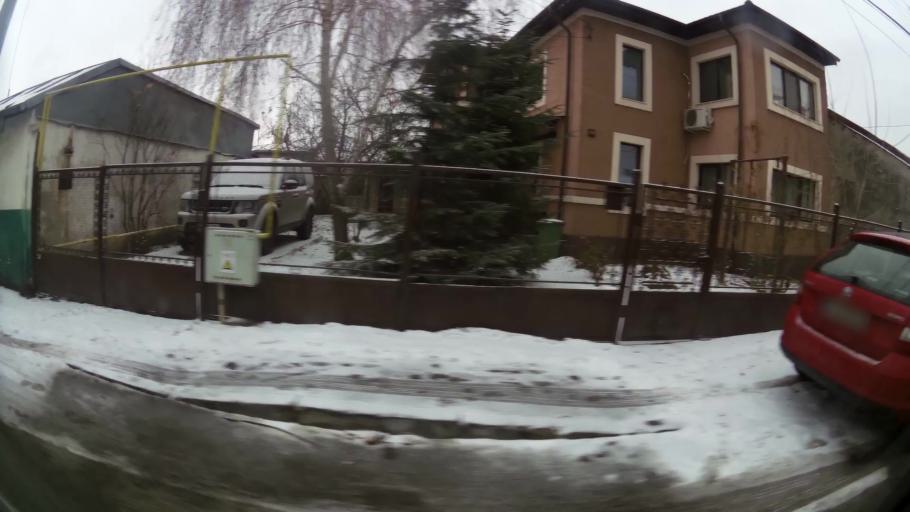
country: RO
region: Prahova
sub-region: Comuna Barcanesti
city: Tatarani
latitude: 44.9316
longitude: 26.0529
